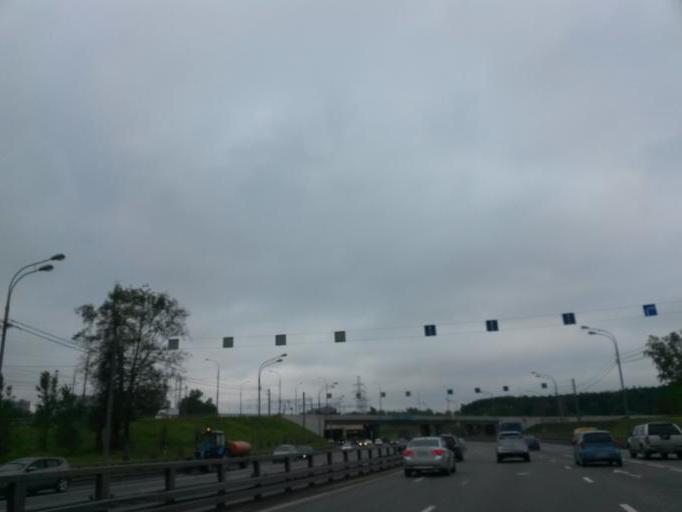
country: RU
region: Moscow
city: Annino
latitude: 55.5590
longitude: 37.5895
